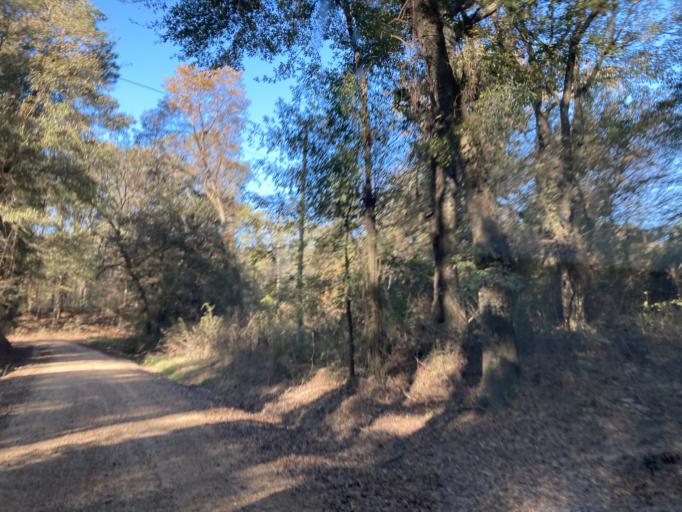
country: US
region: Mississippi
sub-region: Madison County
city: Kearney Park
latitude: 32.7349
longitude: -90.1969
